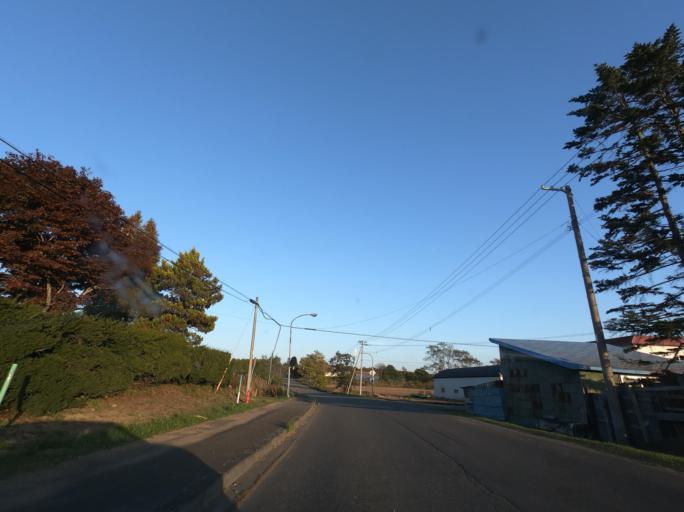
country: JP
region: Hokkaido
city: Chitose
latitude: 42.9280
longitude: 141.7686
